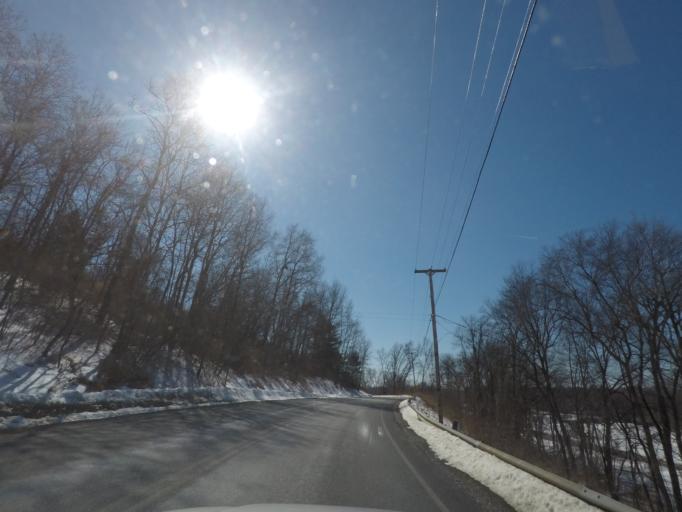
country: US
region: New York
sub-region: Saratoga County
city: Schuylerville
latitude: 43.1127
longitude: -73.5692
